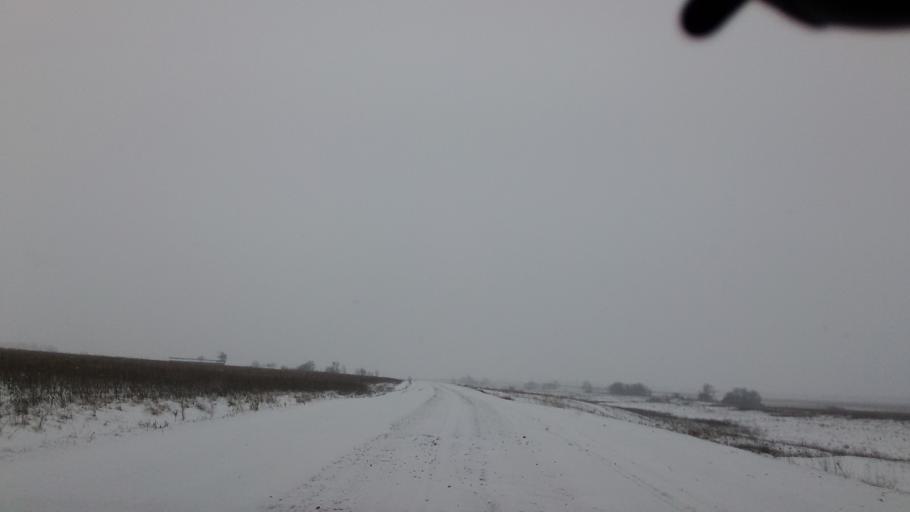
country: RU
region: Tula
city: Volovo
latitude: 53.6831
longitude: 37.9302
